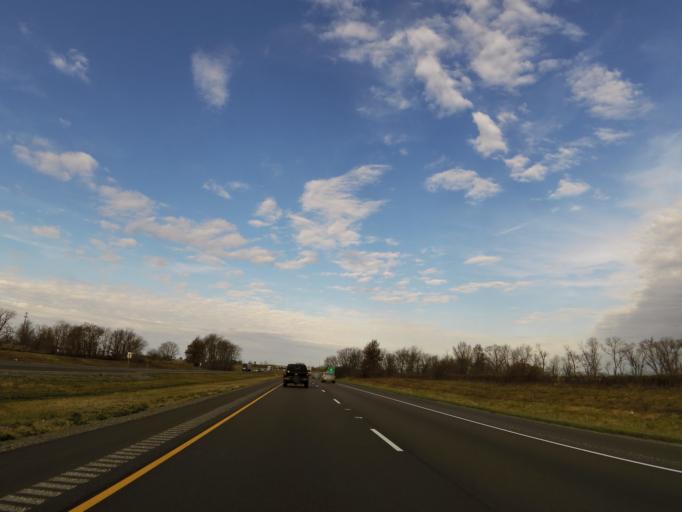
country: US
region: Illinois
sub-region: Washington County
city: Okawville
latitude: 38.4351
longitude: -89.5211
